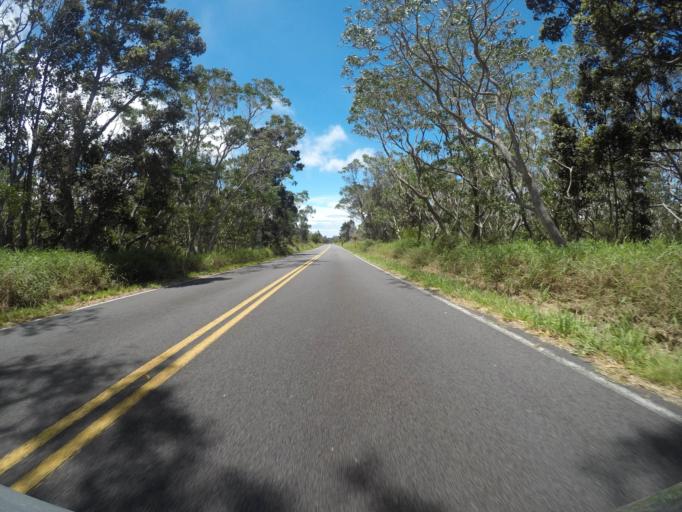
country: US
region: Hawaii
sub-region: Hawaii County
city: Volcano
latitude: 19.3794
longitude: -155.2395
